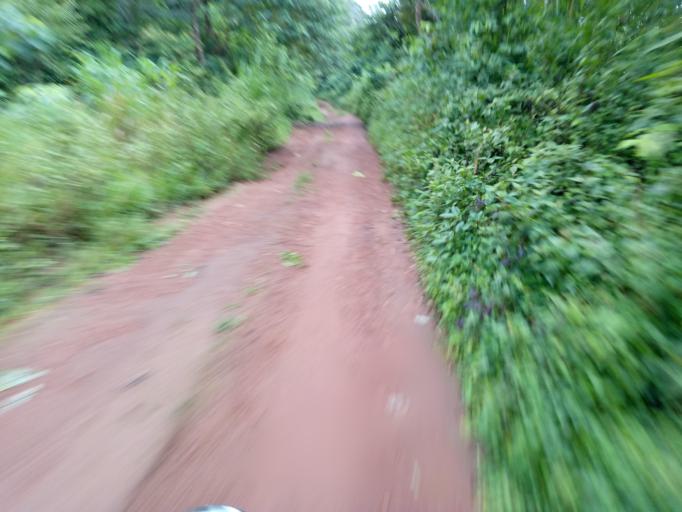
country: SL
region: Eastern Province
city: Buedu
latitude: 8.4695
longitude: -10.3464
